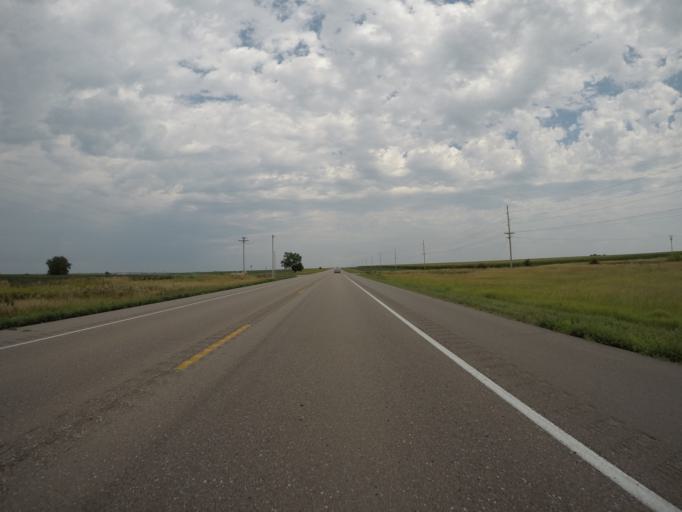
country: US
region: Nebraska
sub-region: Clay County
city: Harvard
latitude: 40.5828
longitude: -98.1480
